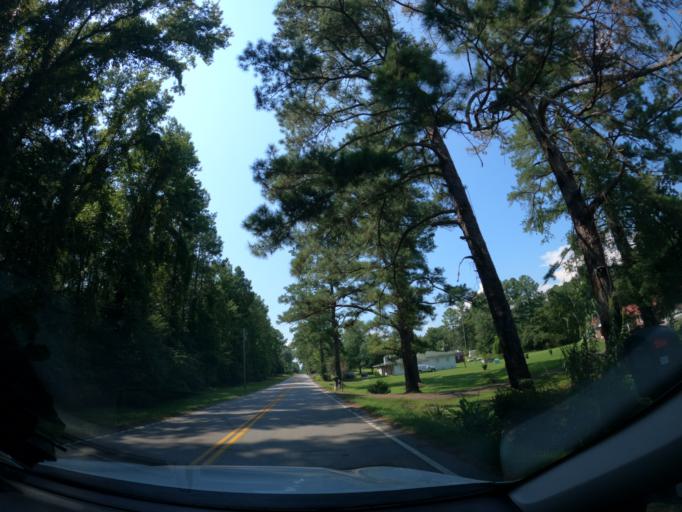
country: US
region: South Carolina
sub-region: Richland County
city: Hopkins
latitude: 33.8428
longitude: -80.8650
